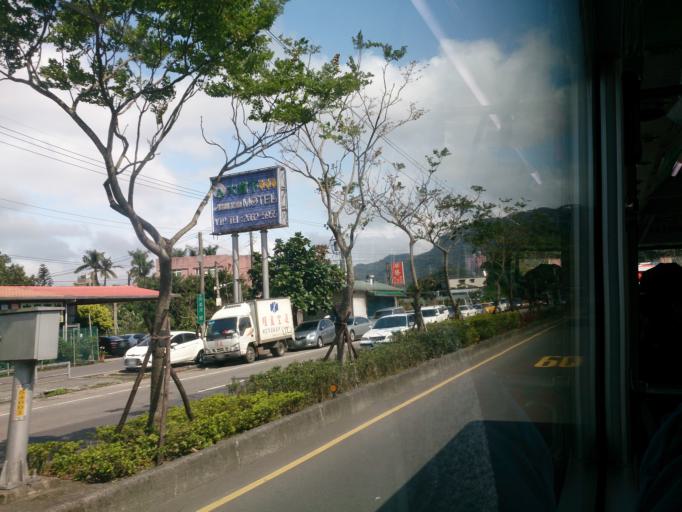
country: TW
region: Taipei
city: Taipei
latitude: 24.9984
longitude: 121.6100
